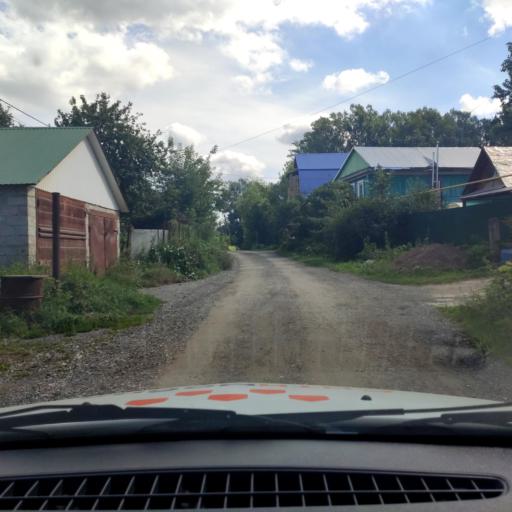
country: RU
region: Bashkortostan
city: Ufa
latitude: 54.7100
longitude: 55.9317
